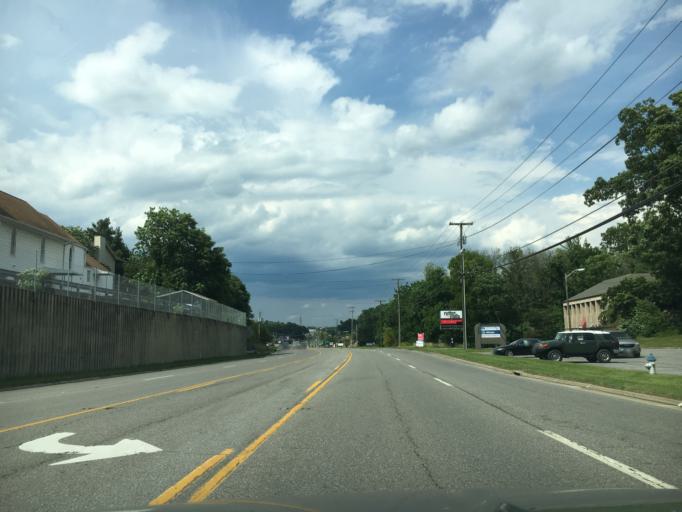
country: US
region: Virginia
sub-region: Roanoke County
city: Cave Spring
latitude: 37.2188
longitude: -80.0167
